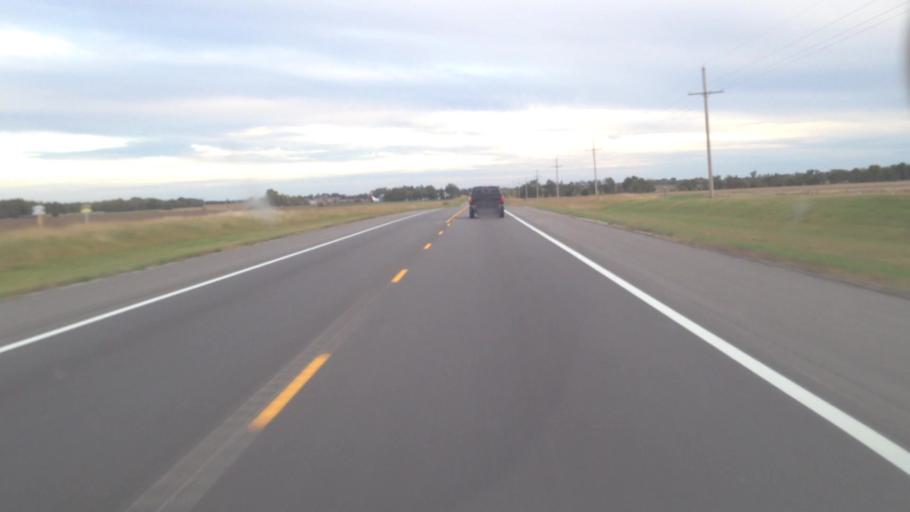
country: US
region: Kansas
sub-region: Franklin County
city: Ottawa
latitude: 38.5340
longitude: -95.2677
